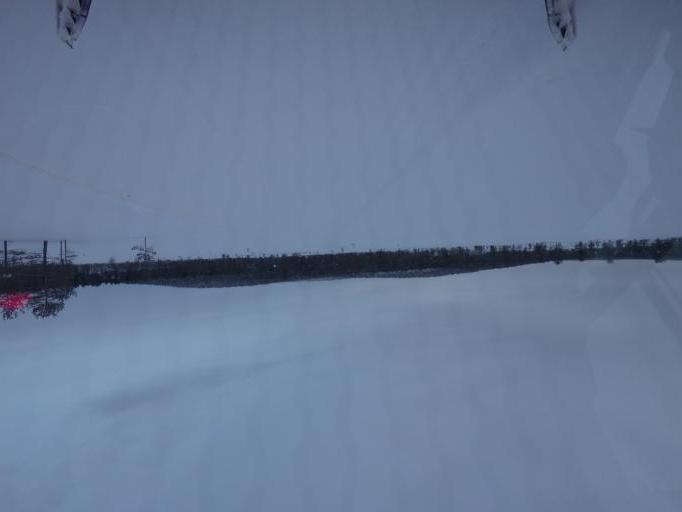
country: FI
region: Lapland
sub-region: Tunturi-Lappi
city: Kolari
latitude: 67.6190
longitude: 24.1324
